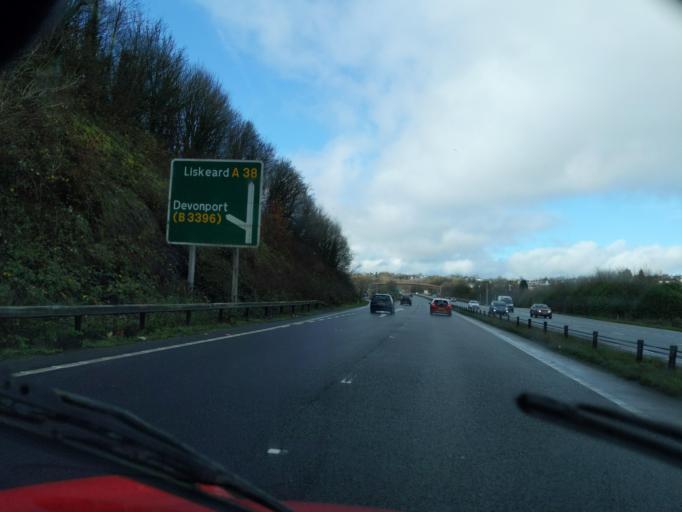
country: GB
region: England
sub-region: Plymouth
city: Plymouth
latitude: 50.4051
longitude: -4.1601
